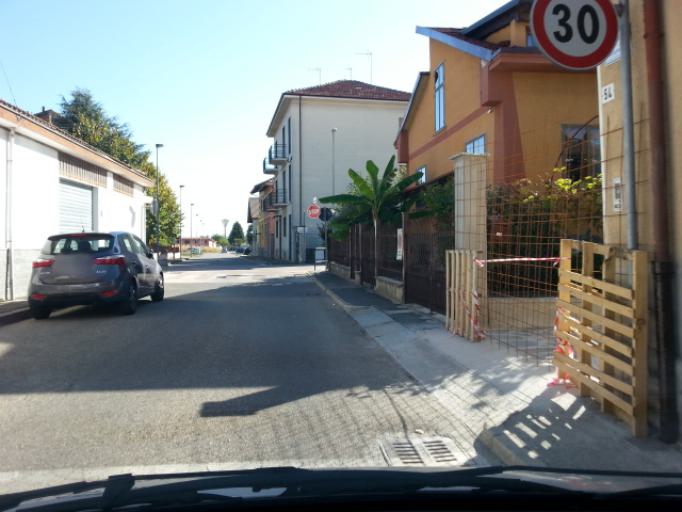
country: IT
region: Piedmont
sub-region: Provincia di Torino
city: Grugliasco
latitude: 45.0590
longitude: 7.5735
